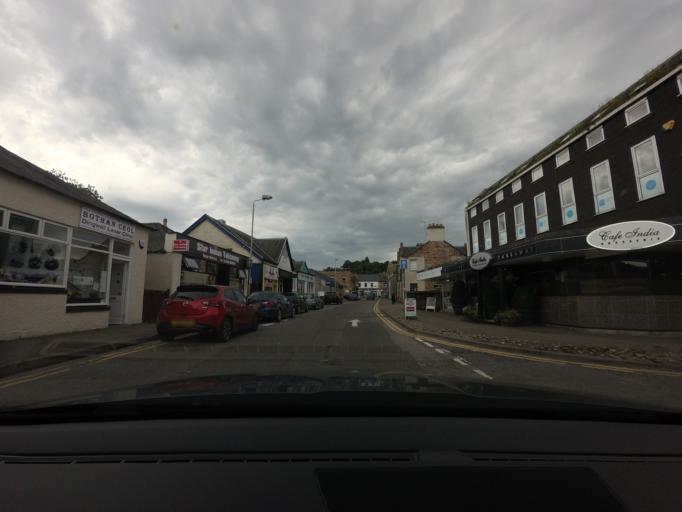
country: GB
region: Scotland
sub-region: Highland
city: Dingwall
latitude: 57.5975
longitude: -4.4284
